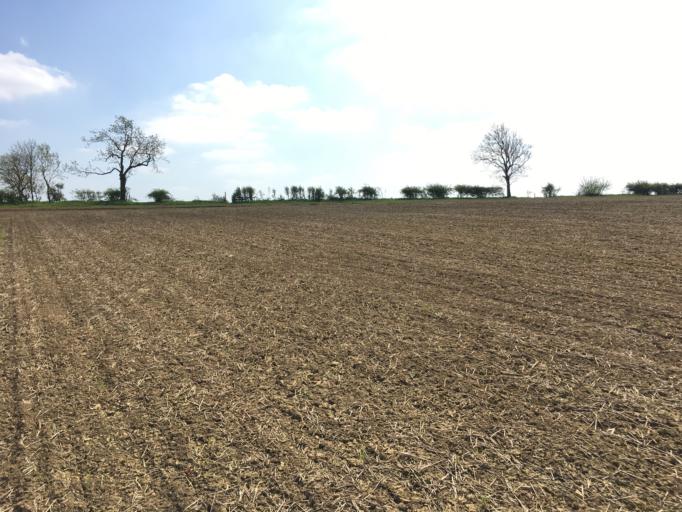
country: GB
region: England
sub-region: Leicestershire
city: Houghton on the Hill
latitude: 52.6103
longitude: -0.9865
